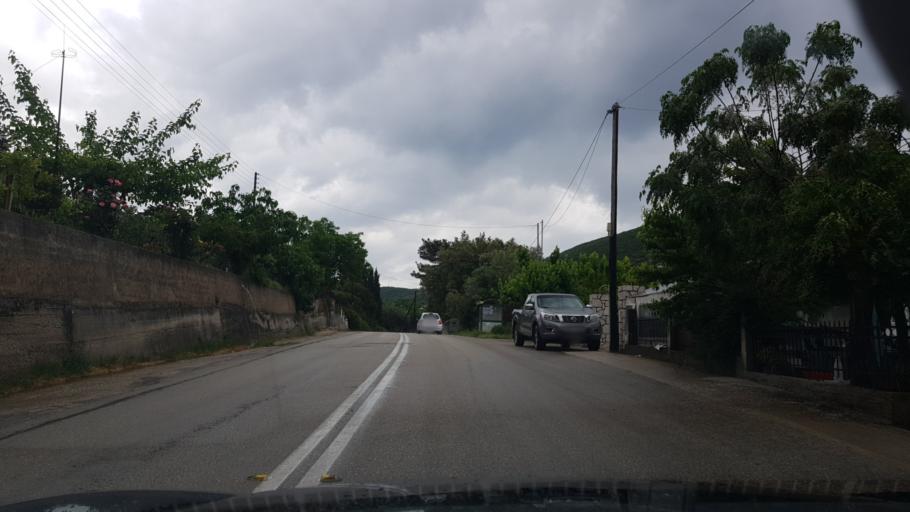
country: GR
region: Ionian Islands
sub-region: Lefkada
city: Nidri
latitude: 38.6293
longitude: 20.6429
